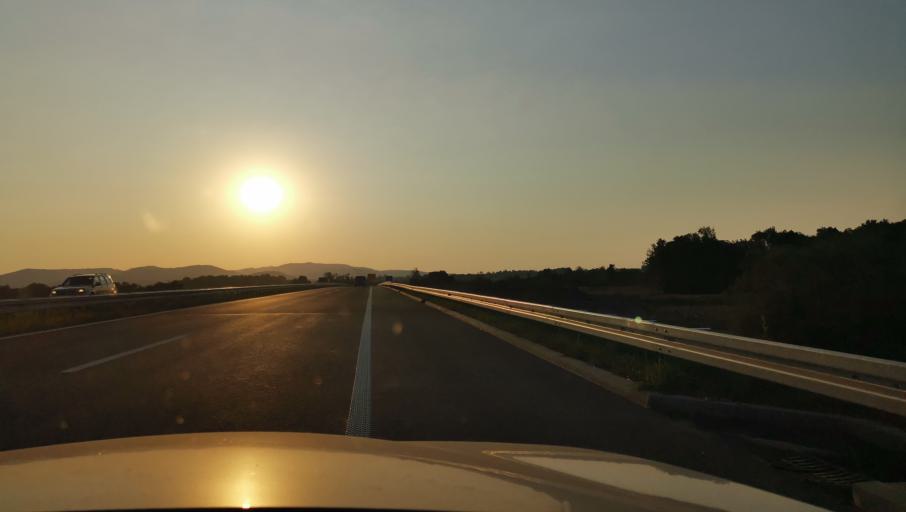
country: RS
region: Central Serbia
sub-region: Kolubarski Okrug
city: Lajkovac
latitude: 44.3550
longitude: 20.1390
